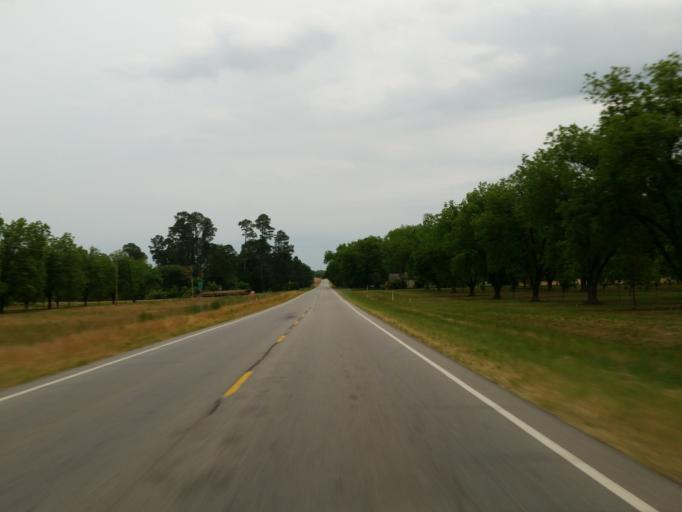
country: US
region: Georgia
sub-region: Dooly County
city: Vienna
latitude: 32.0442
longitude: -83.7956
